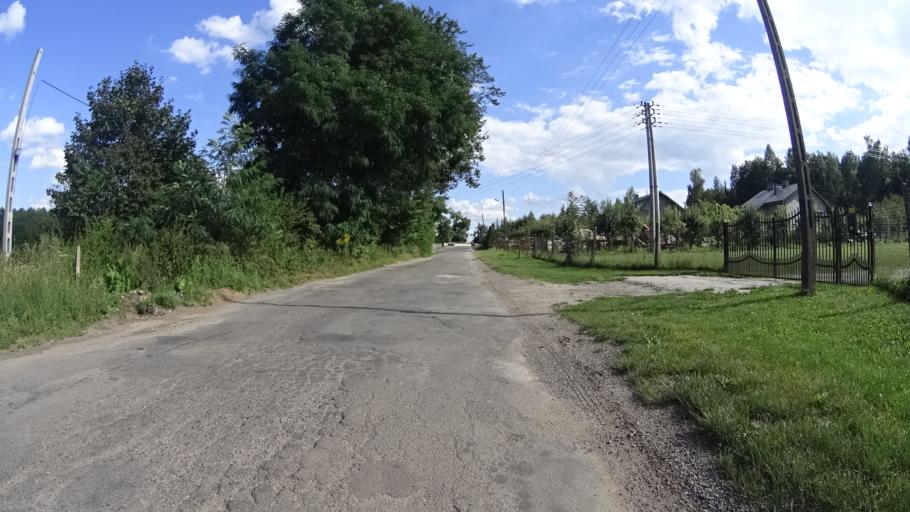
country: PL
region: Masovian Voivodeship
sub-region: Powiat grojecki
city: Mogielnica
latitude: 51.7006
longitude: 20.7118
